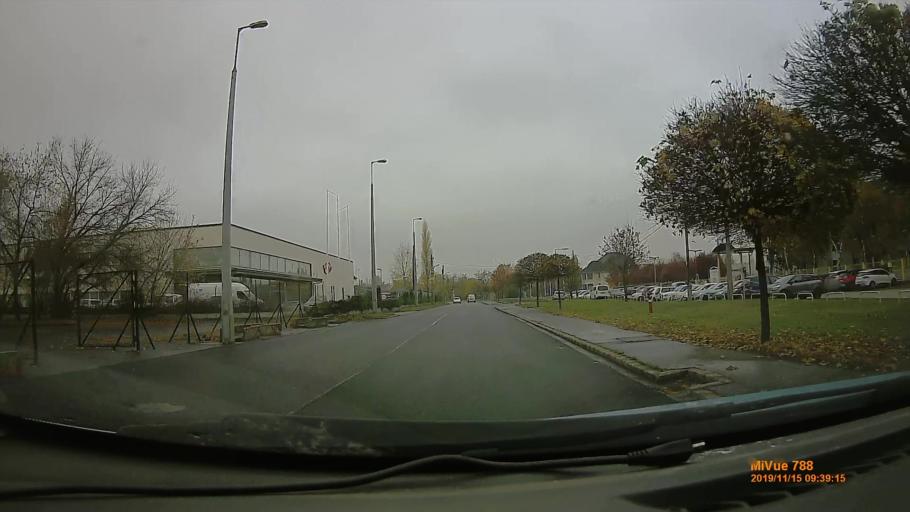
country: HU
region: Budapest
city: Budapest XX. keruelet
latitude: 47.4584
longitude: 19.1026
